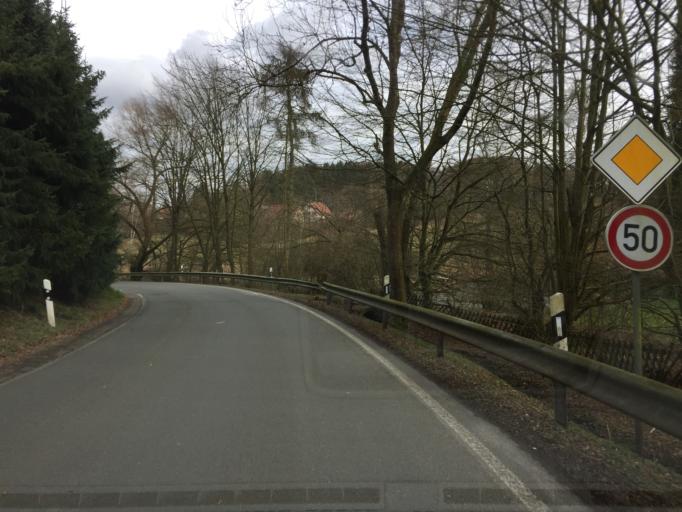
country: DE
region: North Rhine-Westphalia
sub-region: Regierungsbezirk Detmold
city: Detmold
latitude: 51.9003
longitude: 8.8571
